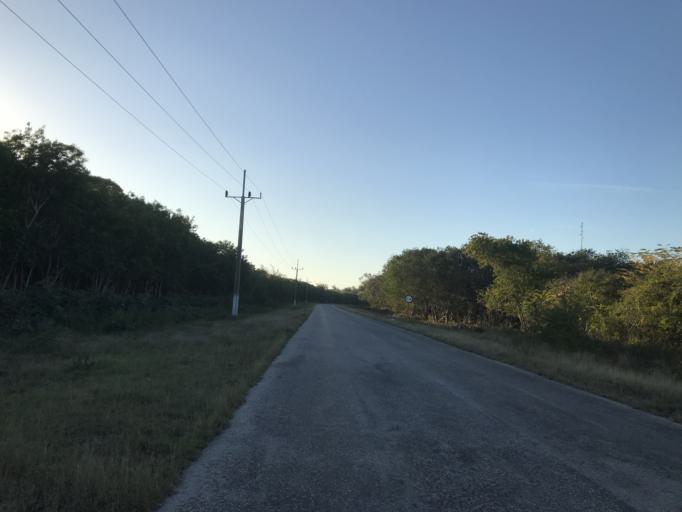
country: CU
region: Cienfuegos
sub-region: Municipio de Aguada de Pasajeros
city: Aguada de Pasajeros
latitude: 22.0673
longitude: -81.0459
